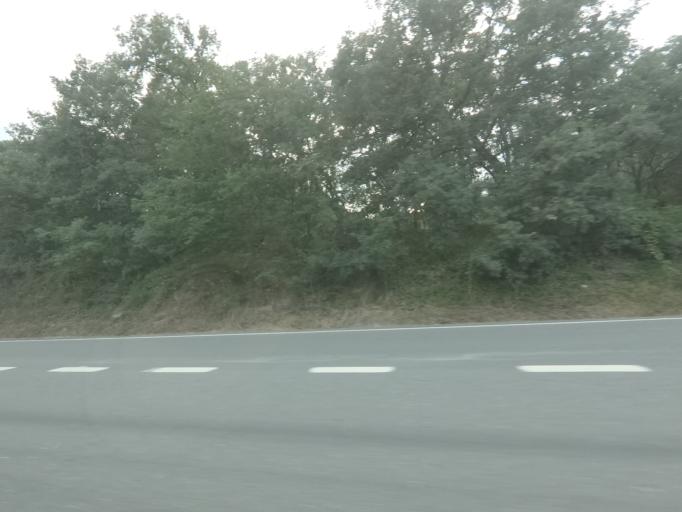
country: ES
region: Galicia
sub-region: Provincia de Ourense
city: Taboadela
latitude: 42.2429
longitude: -7.8431
